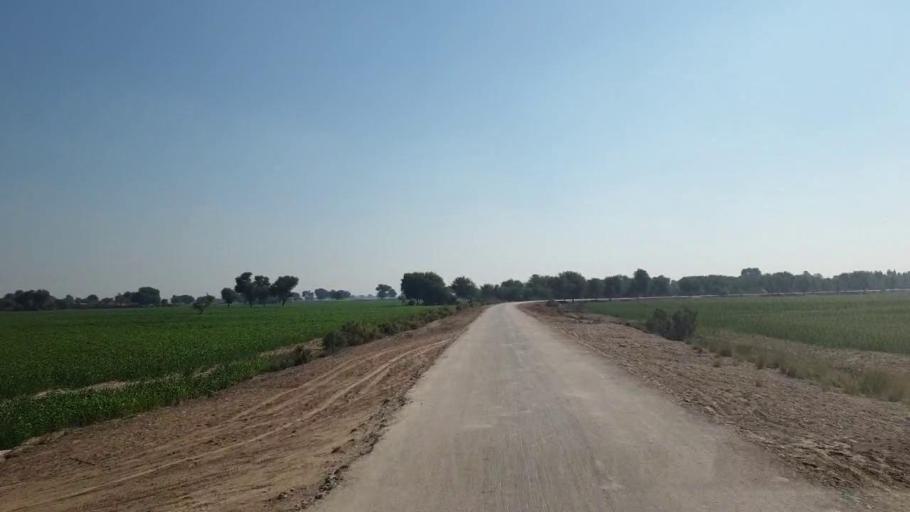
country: PK
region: Sindh
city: Shahpur Chakar
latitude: 26.1199
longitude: 68.6274
